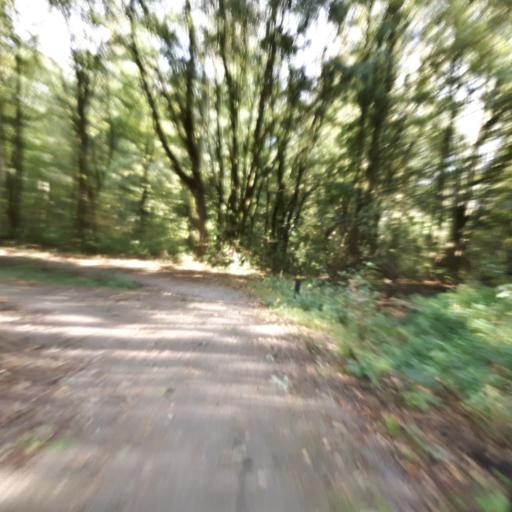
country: NL
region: Zeeland
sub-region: Gemeente Goes
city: Goes
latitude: 51.4912
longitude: 3.8508
